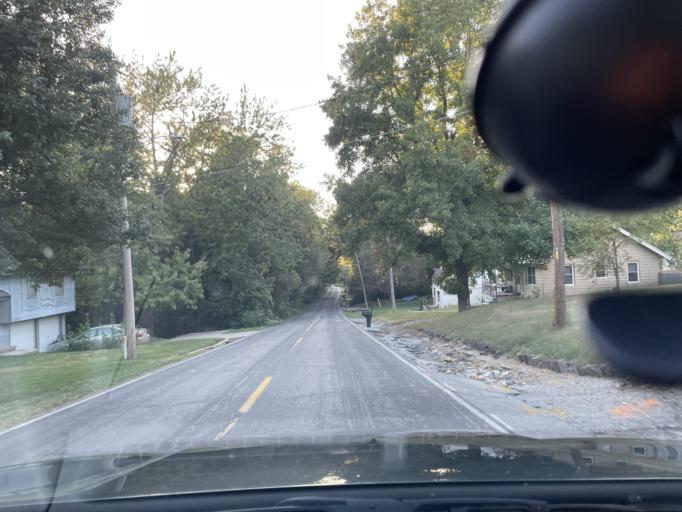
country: US
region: Missouri
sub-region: Andrew County
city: Country Club Village
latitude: 39.7994
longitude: -94.8266
